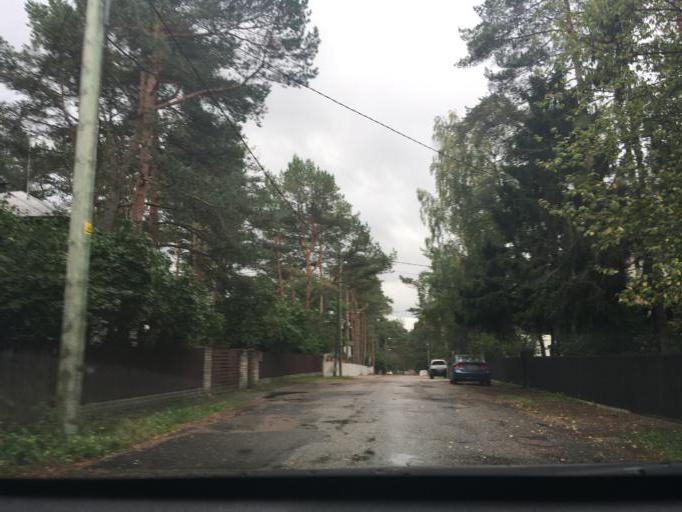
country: EE
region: Harju
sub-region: Saku vald
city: Saku
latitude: 59.3745
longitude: 24.6929
